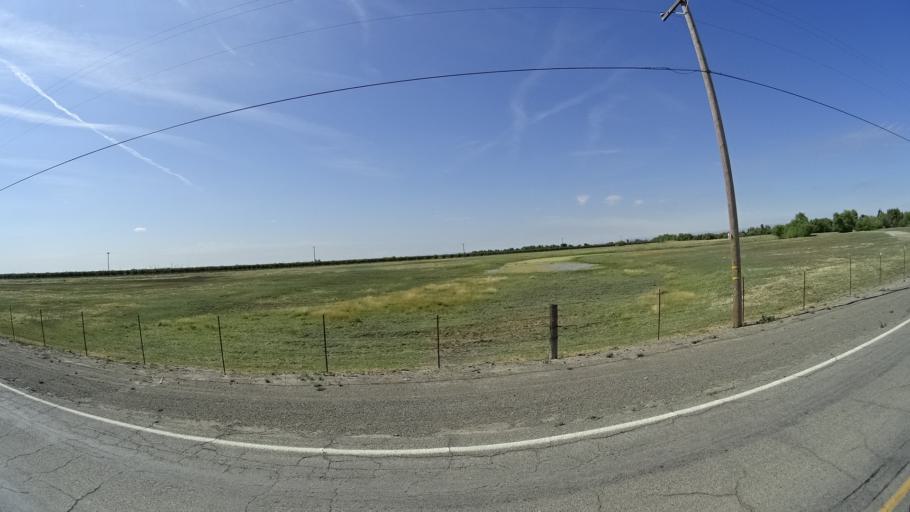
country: US
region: California
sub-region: Kings County
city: Lemoore Station
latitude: 36.2554
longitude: -119.8469
